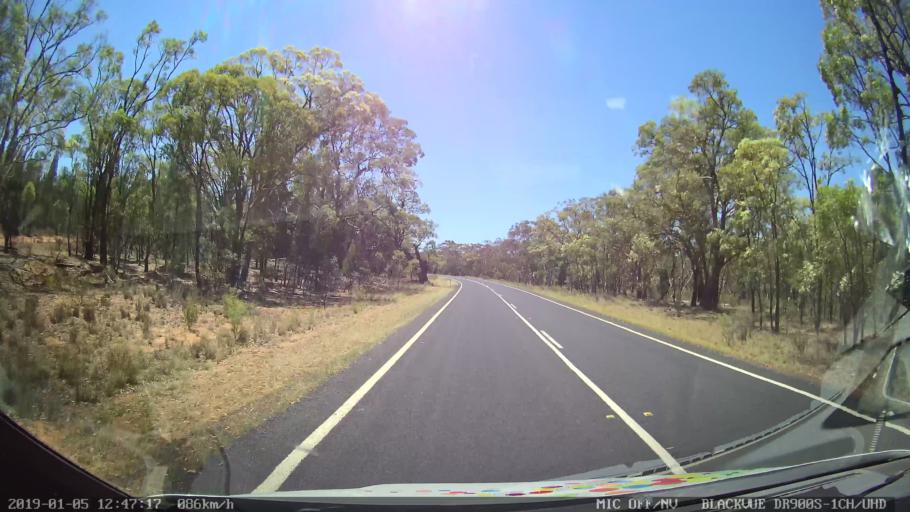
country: AU
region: New South Wales
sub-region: Warrumbungle Shire
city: Coonabarabran
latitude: -31.1174
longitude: 149.5746
